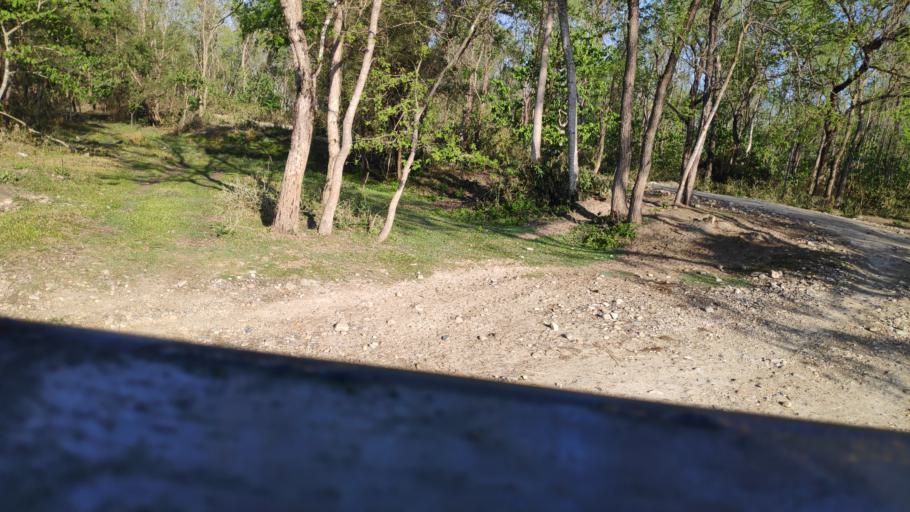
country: NP
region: Central Region
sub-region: Narayani Zone
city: Bharatpur
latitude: 27.5612
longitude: 84.5718
